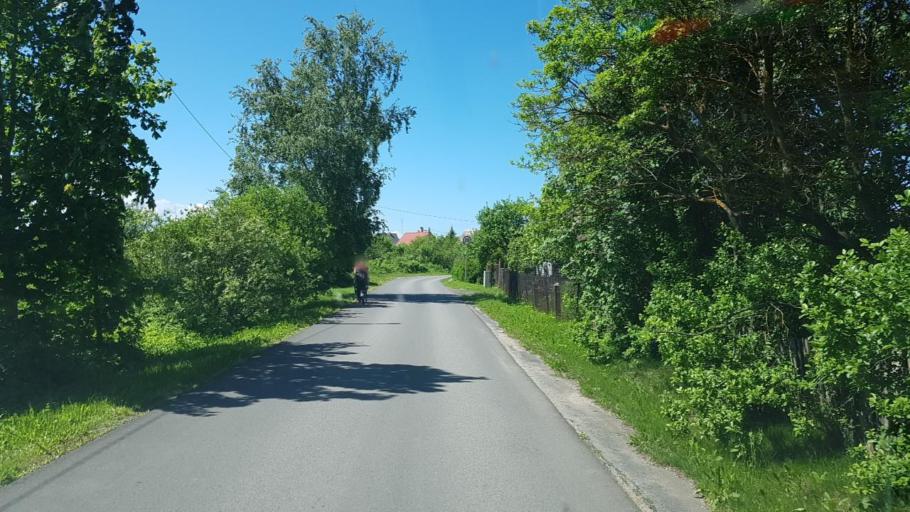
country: EE
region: Ida-Virumaa
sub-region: Narva linn
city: Narva
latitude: 59.3908
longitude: 28.1926
